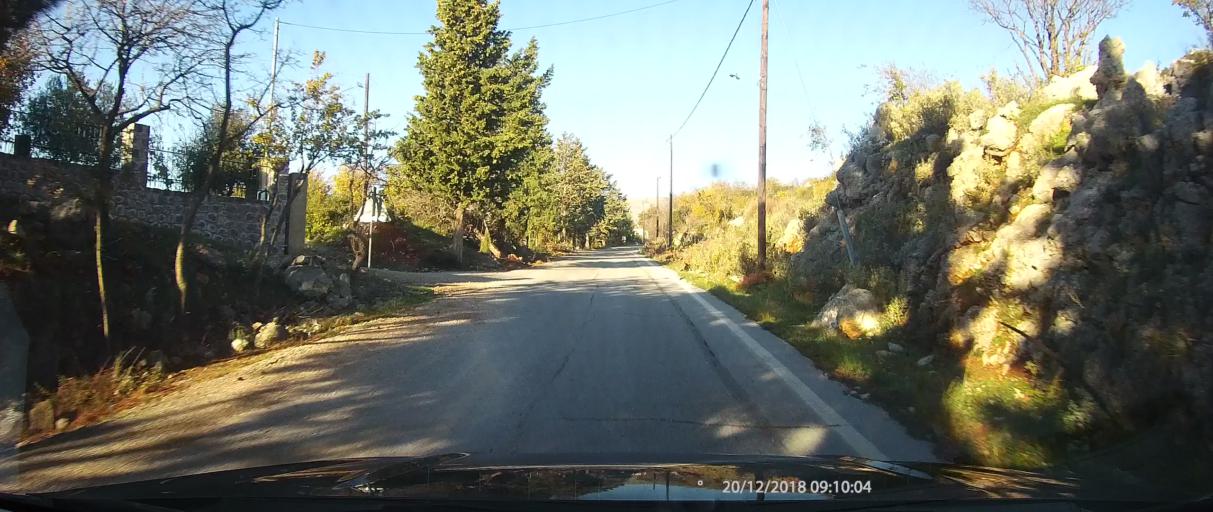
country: GR
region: Peloponnese
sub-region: Nomos Lakonias
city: Sykea
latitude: 36.9138
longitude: 23.0003
